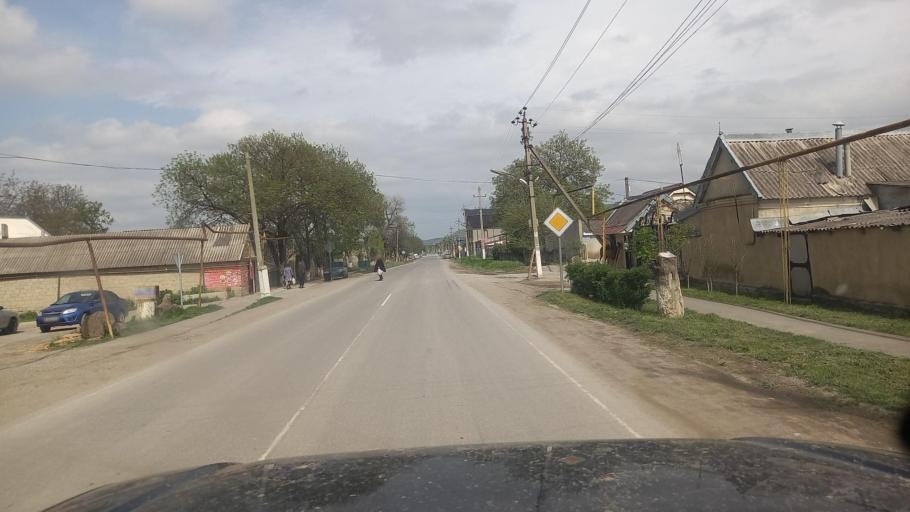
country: RU
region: Kabardino-Balkariya
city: Sarmakovo
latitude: 43.7426
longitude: 43.1947
